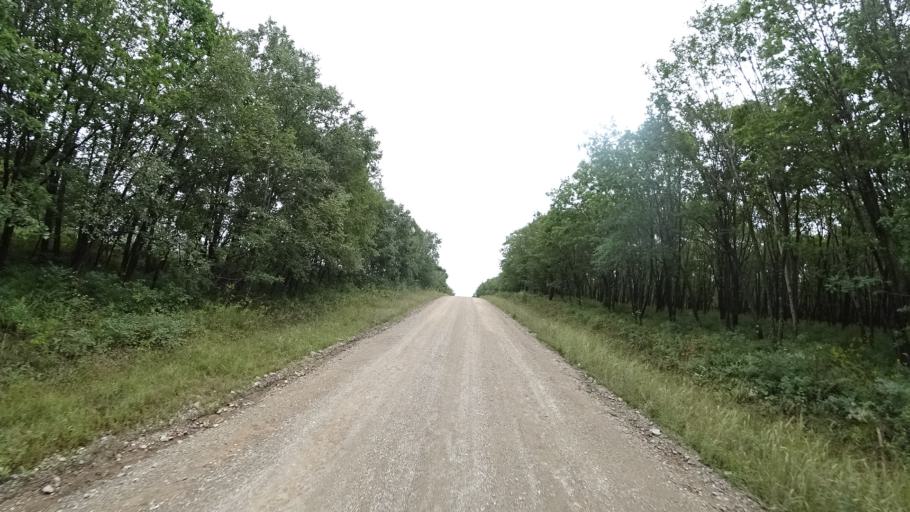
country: RU
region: Primorskiy
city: Ivanovka
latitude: 44.0361
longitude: 132.5006
